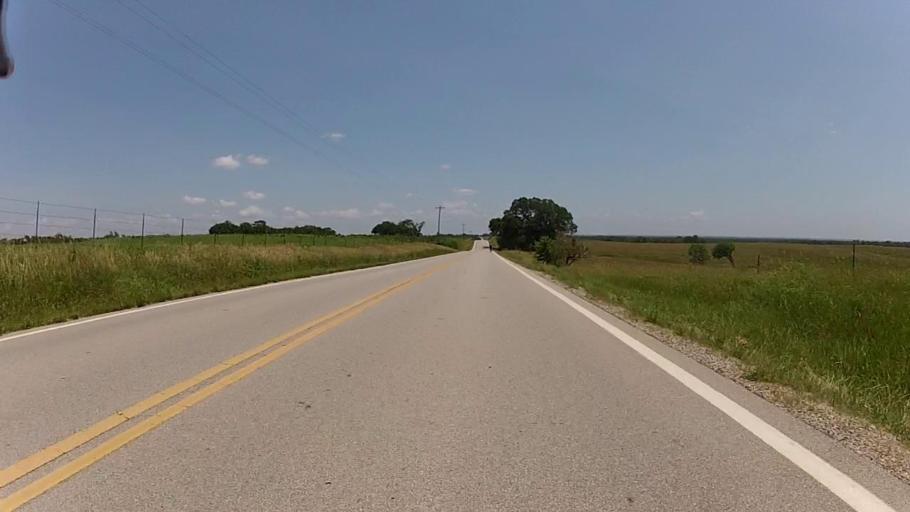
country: US
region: Kansas
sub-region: Montgomery County
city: Cherryvale
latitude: 37.1934
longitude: -95.5022
